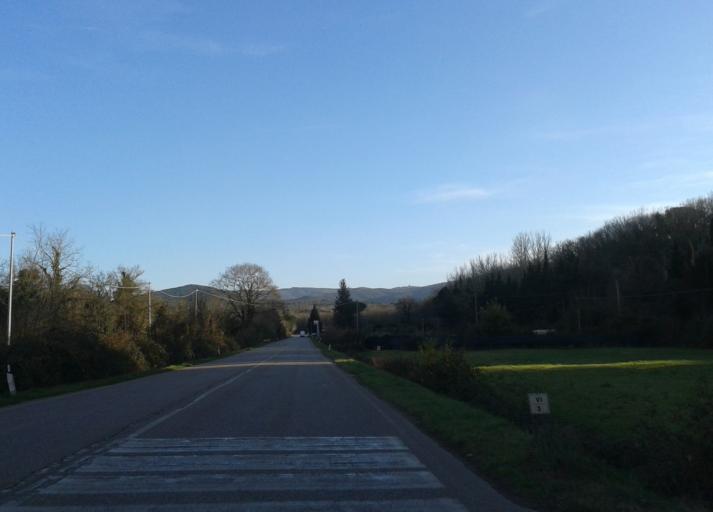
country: IT
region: Tuscany
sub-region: Provincia di Livorno
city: Guasticce
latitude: 43.5716
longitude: 10.3764
